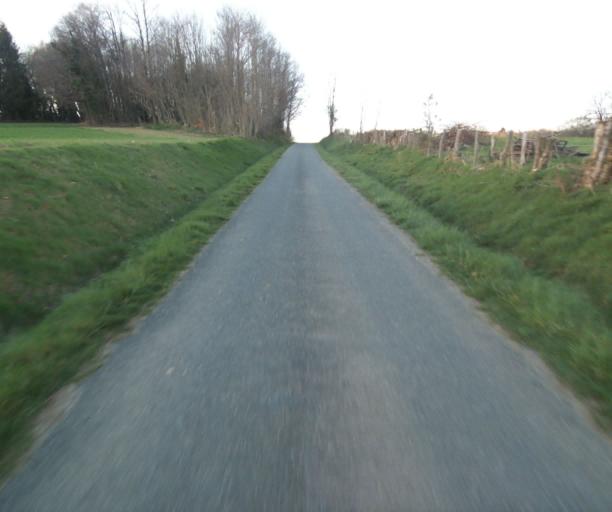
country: FR
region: Limousin
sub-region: Departement de la Correze
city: Uzerche
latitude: 45.3801
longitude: 1.6031
